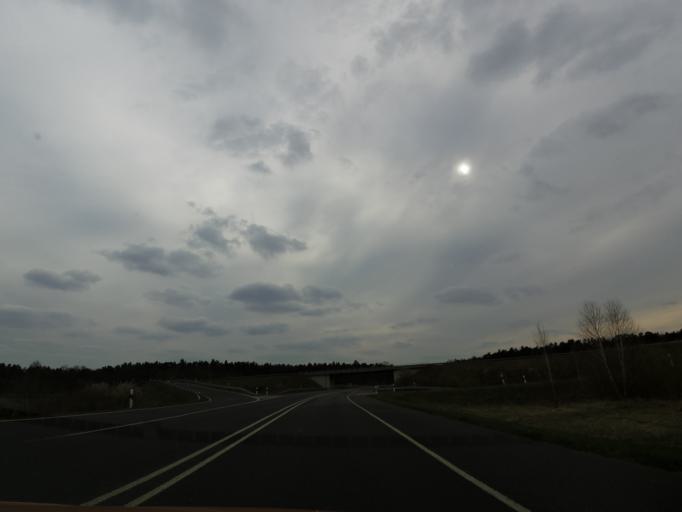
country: DE
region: Brandenburg
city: Mullrose
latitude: 52.2382
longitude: 14.3950
